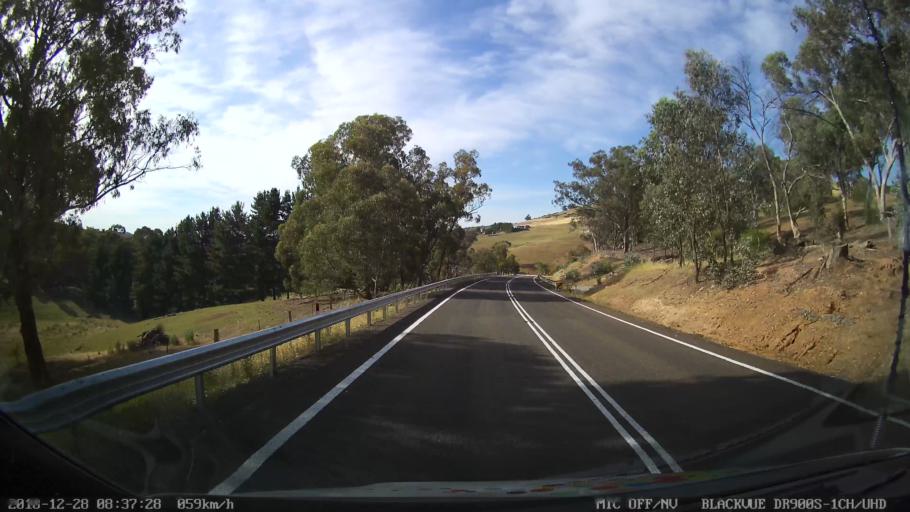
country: AU
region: New South Wales
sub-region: Blayney
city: Blayney
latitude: -33.9956
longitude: 149.3131
